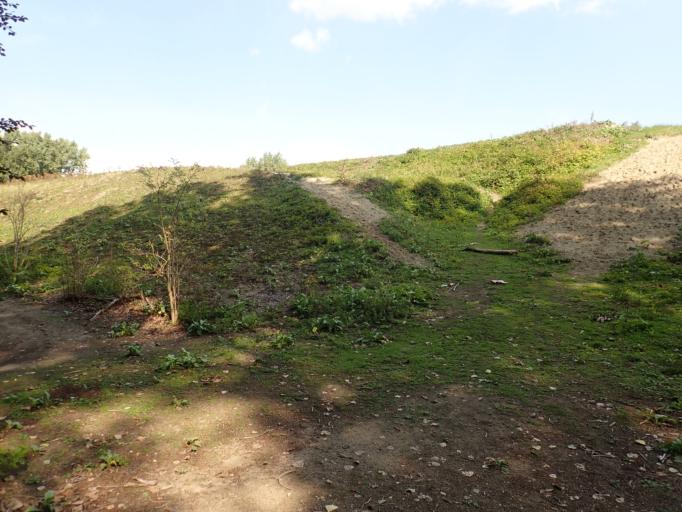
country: BE
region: Flanders
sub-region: Provincie Antwerpen
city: Antwerpen
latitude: 51.2296
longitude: 4.3731
